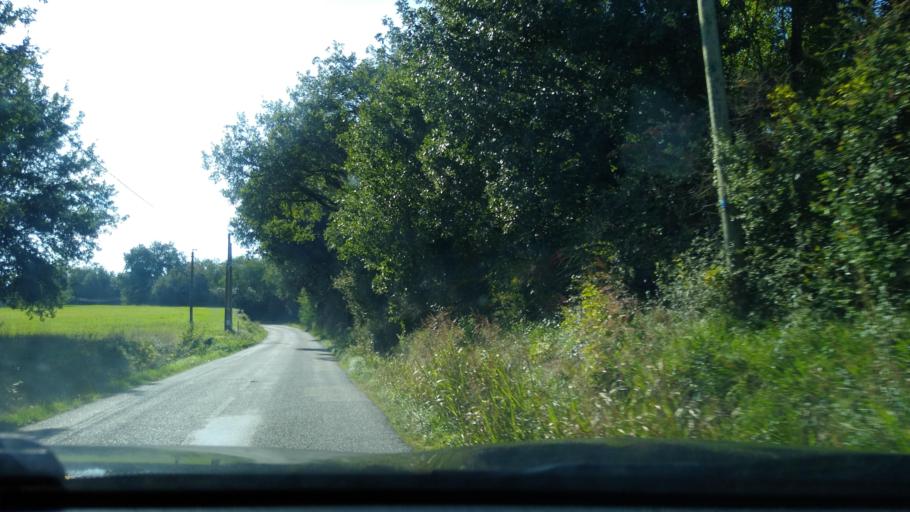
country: FR
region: Midi-Pyrenees
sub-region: Departement de la Haute-Garonne
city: Grenade
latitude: 43.7521
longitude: 1.2523
